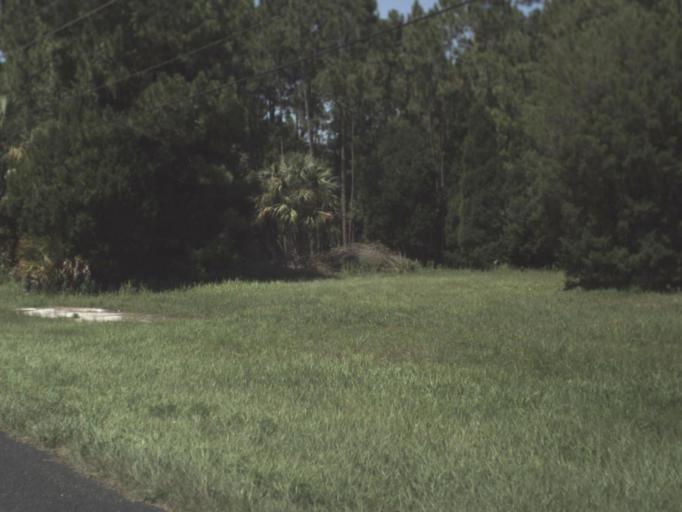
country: US
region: Florida
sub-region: Citrus County
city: Homosassa Springs
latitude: 28.8117
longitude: -82.5765
